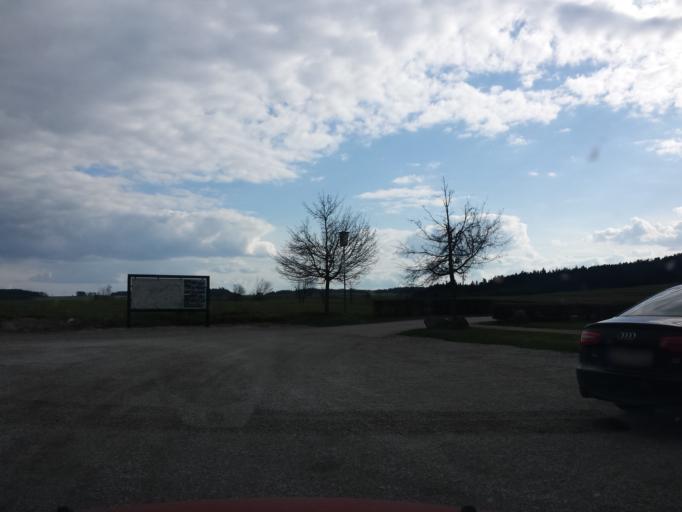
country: AT
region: Lower Austria
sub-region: Politischer Bezirk Krems
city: Rastenfeld
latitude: 48.5358
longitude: 15.3532
